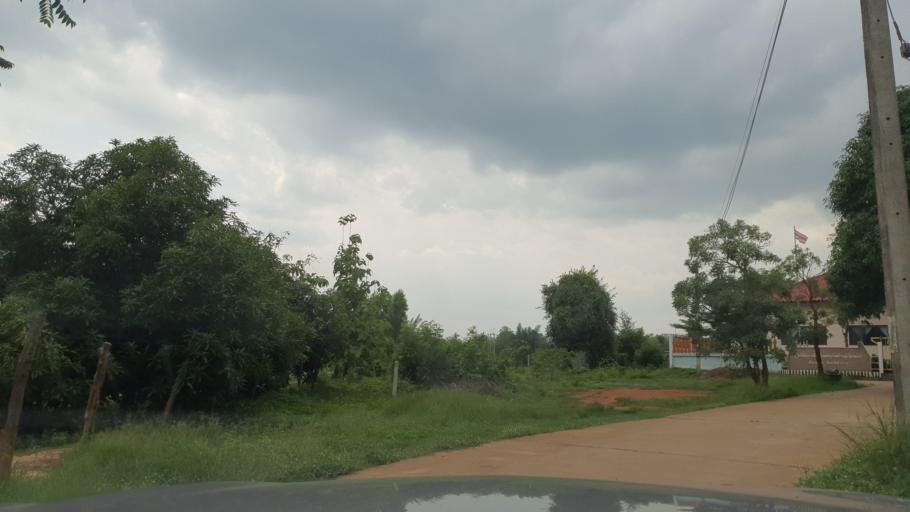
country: TH
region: Sukhothai
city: Thung Saliam
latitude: 17.3291
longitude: 99.4553
